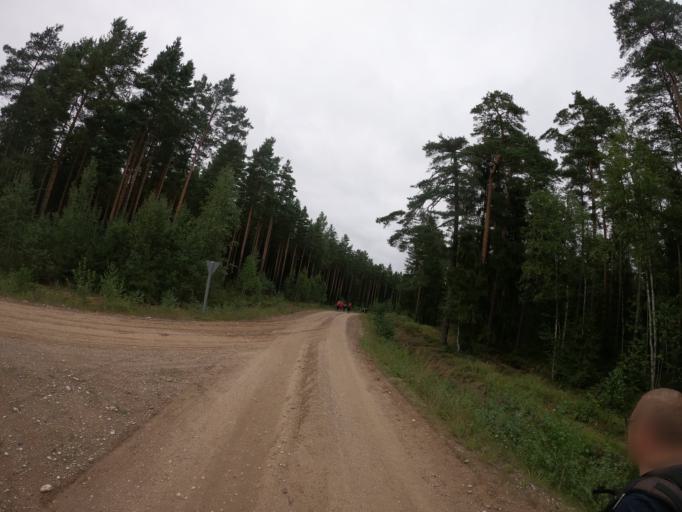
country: LV
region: Kuldigas Rajons
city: Kuldiga
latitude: 57.0233
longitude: 22.0068
